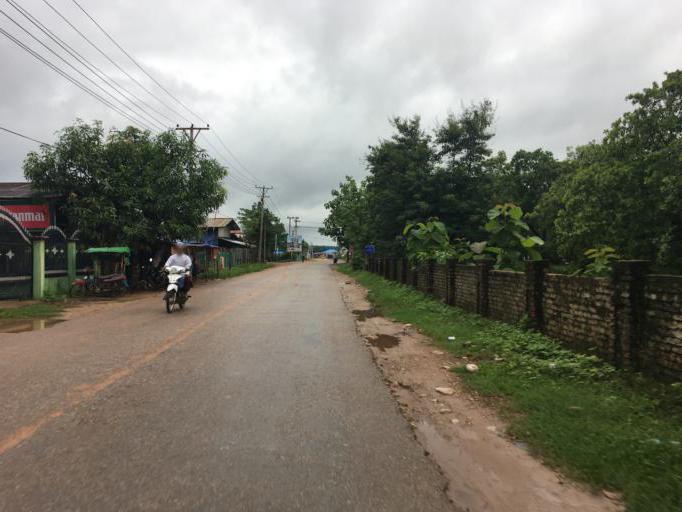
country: MM
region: Mon
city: Mudon
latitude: 16.0444
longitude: 98.1173
